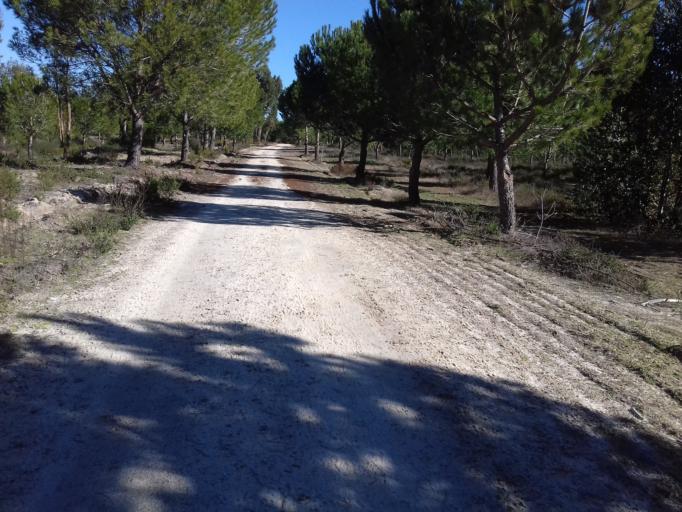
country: PT
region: Santarem
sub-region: Coruche
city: Coruche
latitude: 39.0201
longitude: -8.5482
